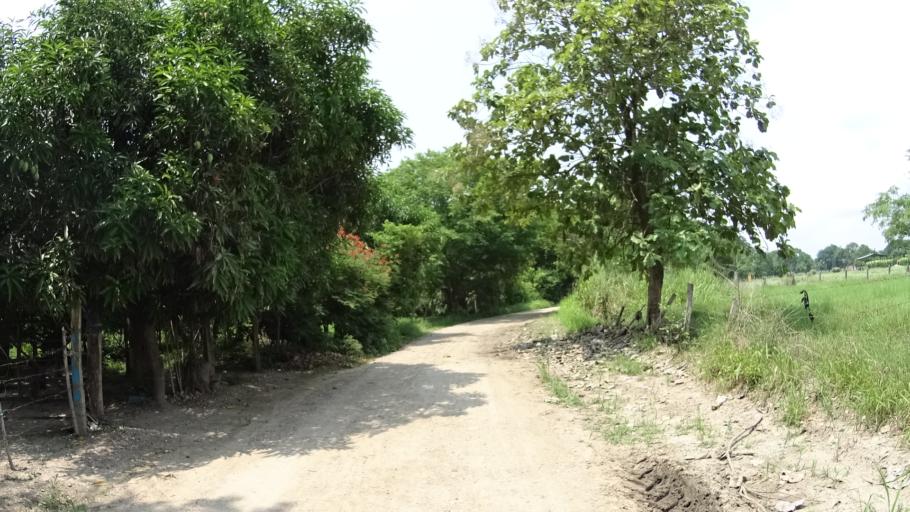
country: CO
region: Cundinamarca
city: Puerto Salgar
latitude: 5.5277
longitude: -74.6849
